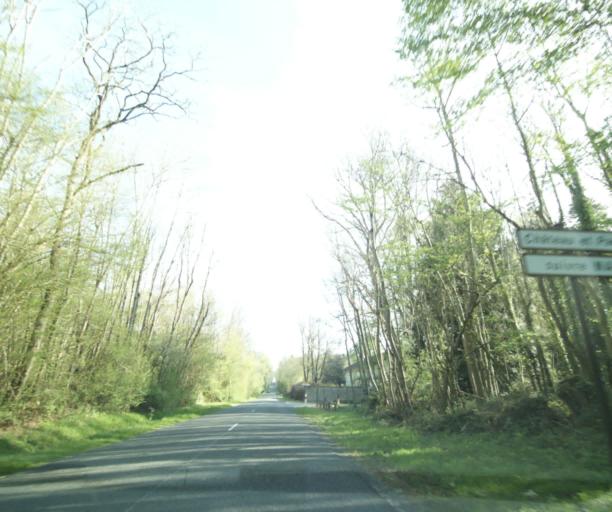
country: FR
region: Ile-de-France
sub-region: Departement de Seine-et-Marne
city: Nangis
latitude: 48.5290
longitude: 2.9787
